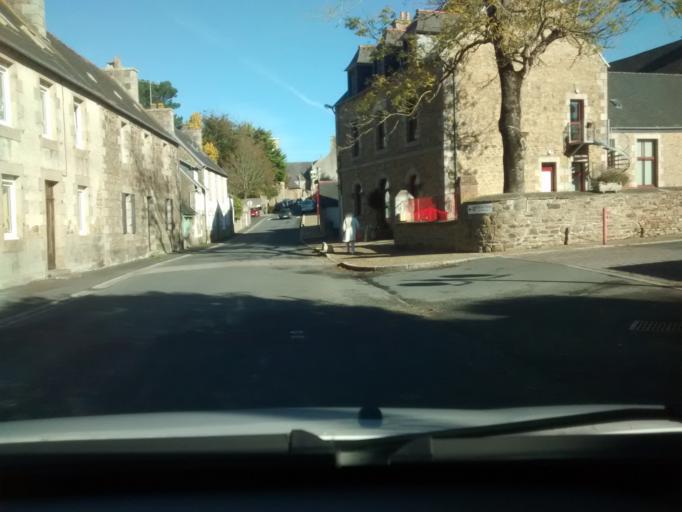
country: FR
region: Brittany
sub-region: Departement des Cotes-d'Armor
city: Louannec
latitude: 48.7926
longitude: -3.4119
